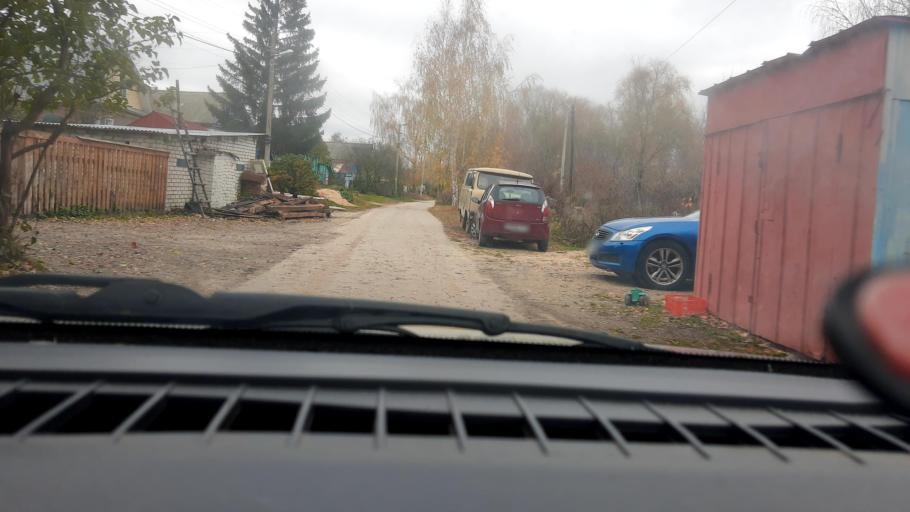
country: RU
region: Nizjnij Novgorod
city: Afonino
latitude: 56.2716
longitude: 44.1049
